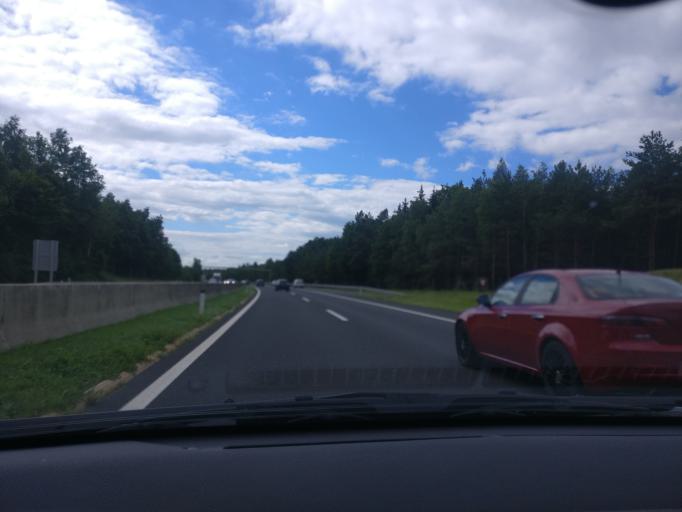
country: AT
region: Burgenland
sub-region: Politischer Bezirk Oberwart
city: Grafenschachen
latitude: 47.3940
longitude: 16.0818
